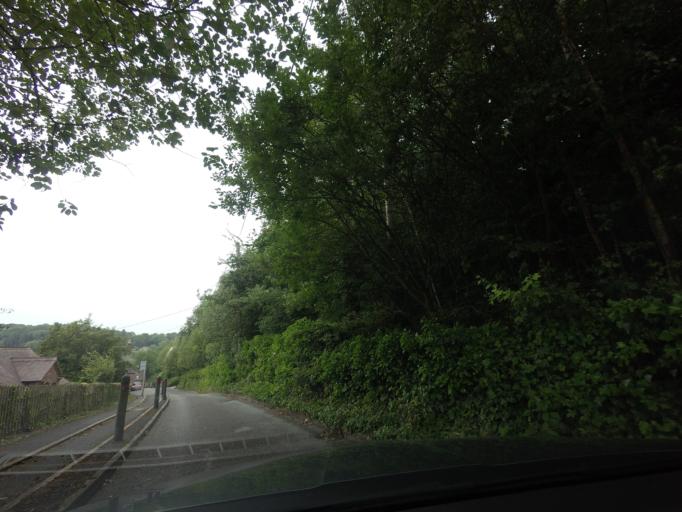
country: GB
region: England
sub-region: Telford and Wrekin
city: Ironbridge
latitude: 52.6420
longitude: -2.4858
